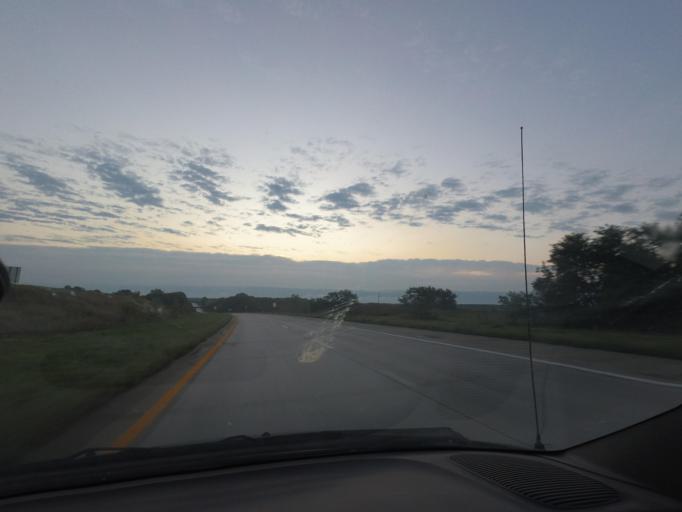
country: US
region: Missouri
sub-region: Macon County
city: Macon
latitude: 39.7541
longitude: -92.6150
